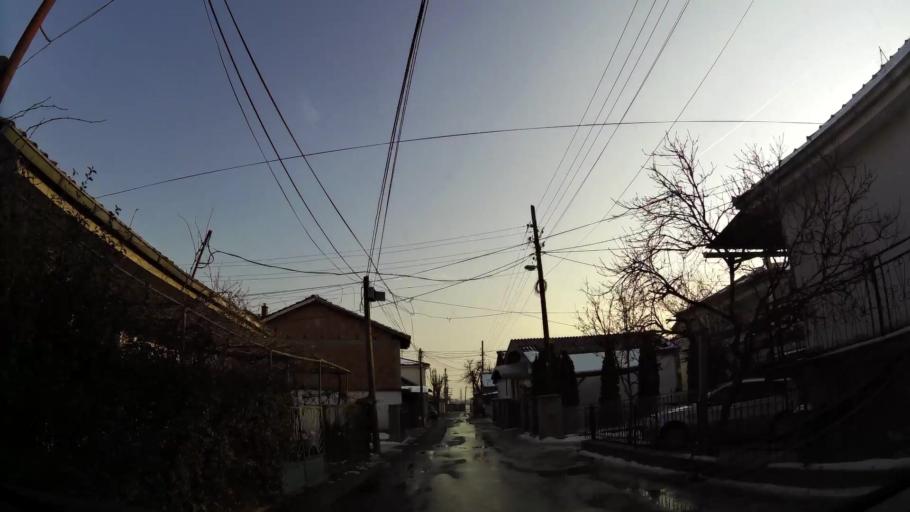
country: MK
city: Creshevo
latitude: 42.0230
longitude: 21.5205
